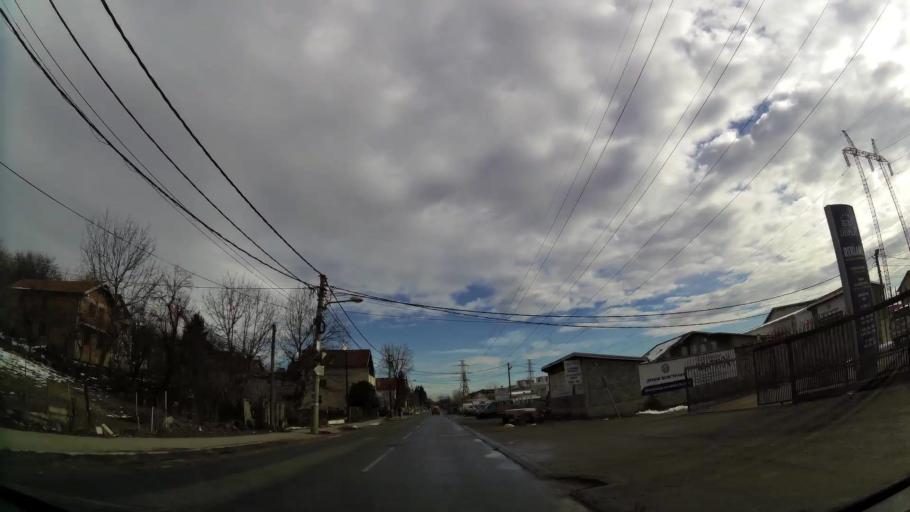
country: RS
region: Central Serbia
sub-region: Belgrade
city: Zemun
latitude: 44.8004
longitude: 20.3573
